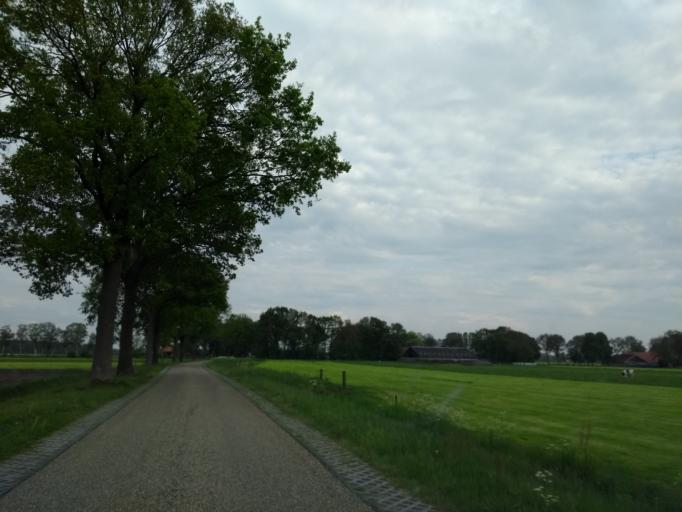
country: NL
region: Overijssel
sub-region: Gemeente Twenterand
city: Vriezenveen
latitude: 52.4088
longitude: 6.6708
